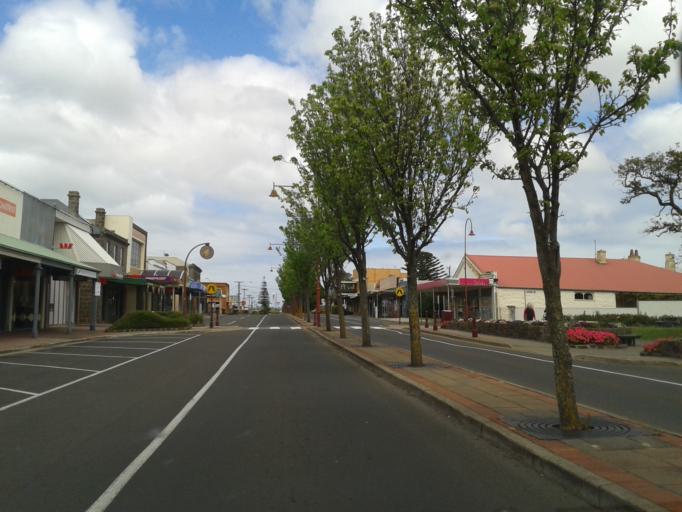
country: AU
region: Victoria
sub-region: Glenelg
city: Portland
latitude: -38.3469
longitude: 141.6038
